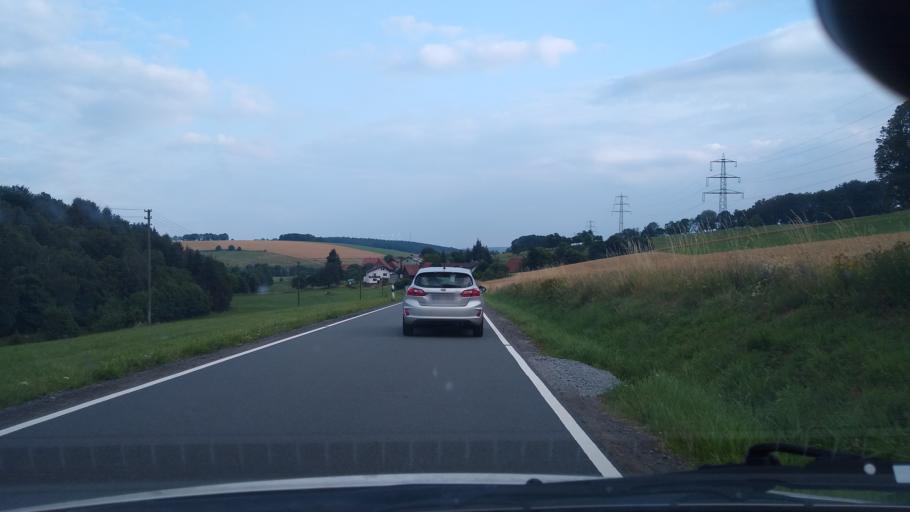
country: DE
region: Hesse
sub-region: Regierungsbezirk Darmstadt
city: Frankisch-Crumbach
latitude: 49.6915
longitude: 8.9179
